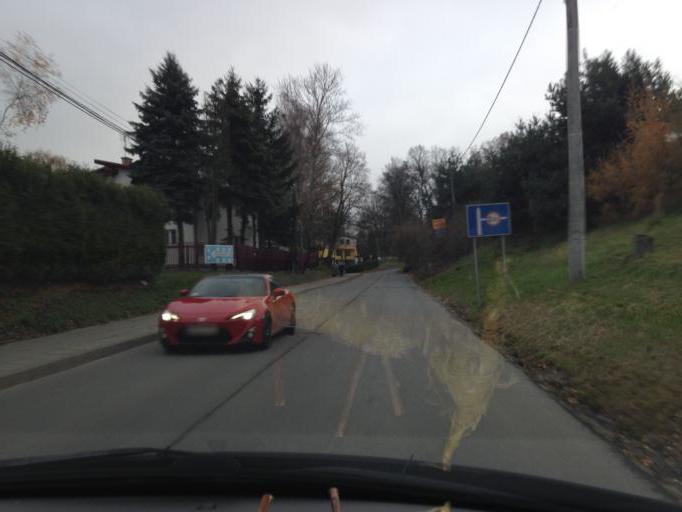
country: PL
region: Lesser Poland Voivodeship
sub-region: Powiat krakowski
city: Wrzasowice
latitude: 50.0038
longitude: 19.9492
